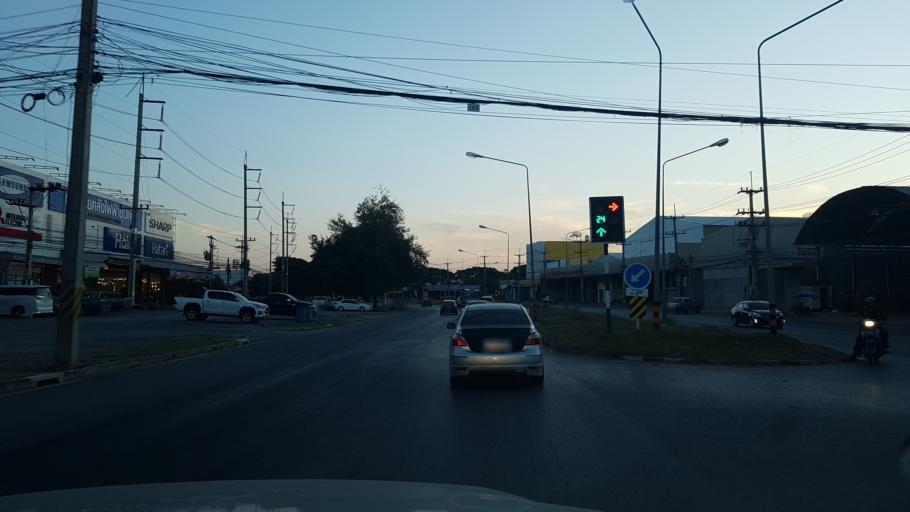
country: TH
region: Khon Kaen
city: Chum Phae
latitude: 16.5366
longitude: 102.1064
